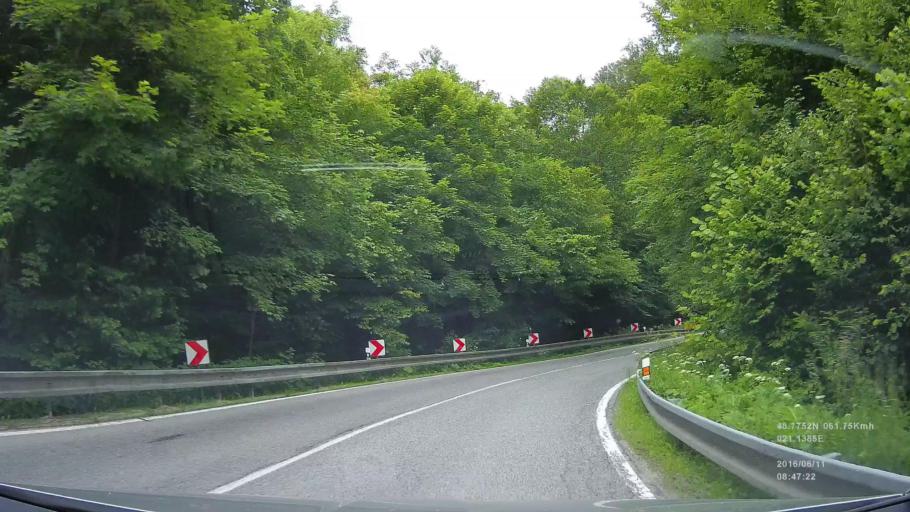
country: SK
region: Kosicky
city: Kosice
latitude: 48.7653
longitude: 21.1727
